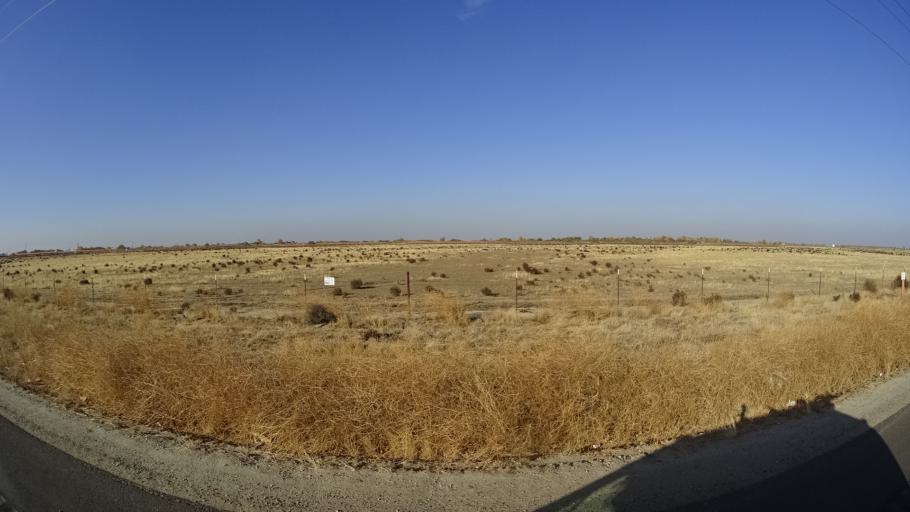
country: US
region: California
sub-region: Kern County
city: Rosedale
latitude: 35.2962
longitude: -119.2488
